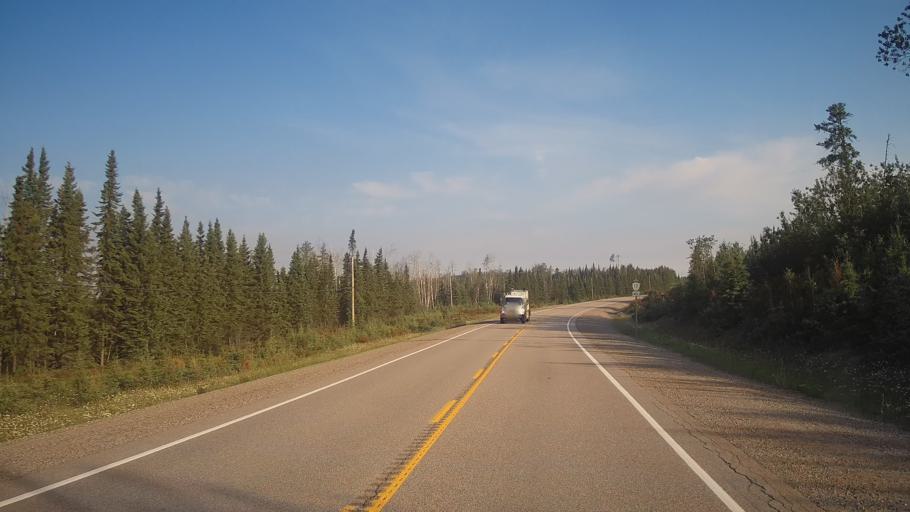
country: CA
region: Ontario
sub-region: Rainy River District
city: Atikokan
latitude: 49.3885
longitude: -91.5992
